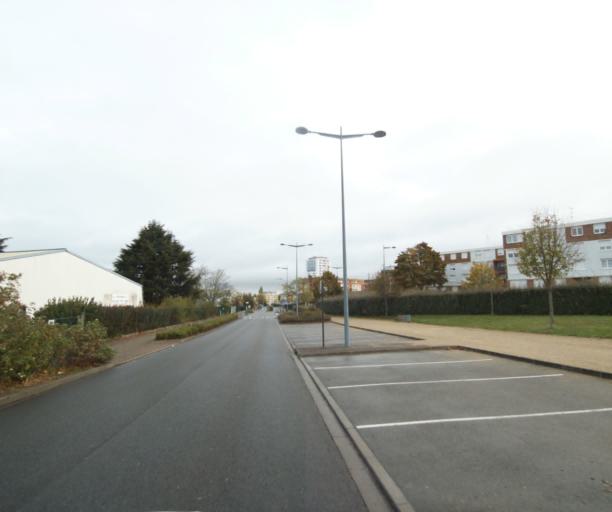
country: FR
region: Centre
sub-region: Departement d'Eure-et-Loir
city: Luray
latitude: 48.7354
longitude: 1.3877
